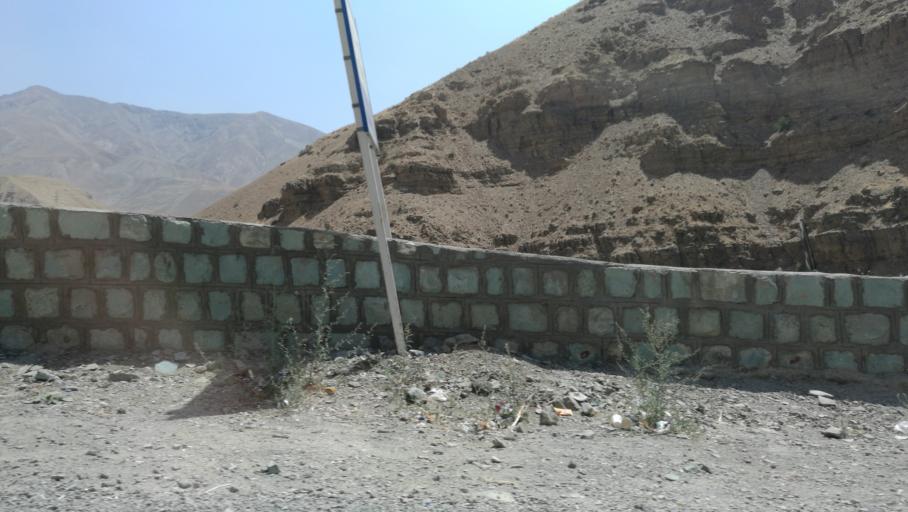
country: IR
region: Alborz
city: Karaj
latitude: 35.9466
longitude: 51.0717
